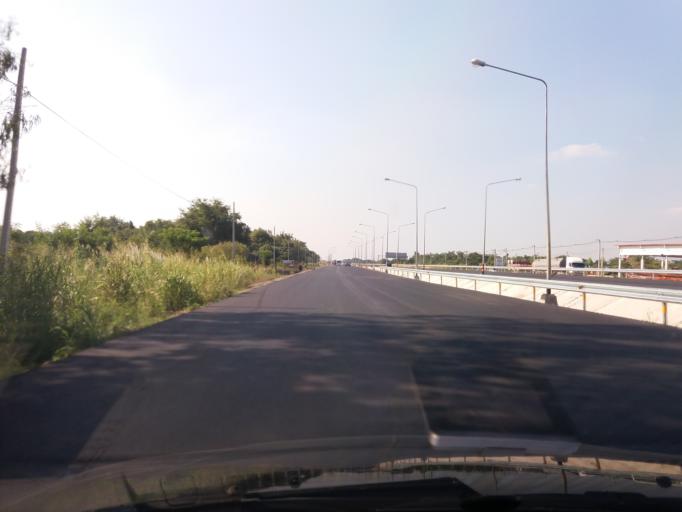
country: TH
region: Nakhon Sawan
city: Krok Phra
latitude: 15.6212
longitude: 100.1149
